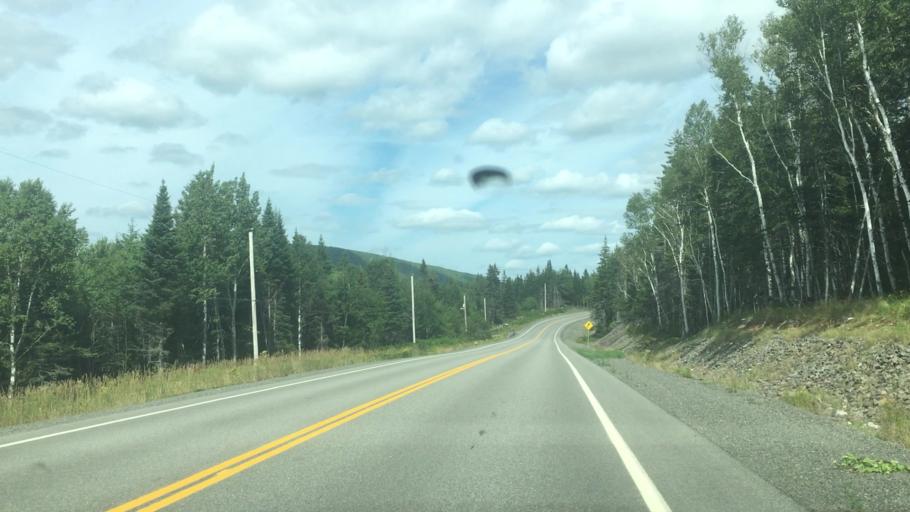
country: CA
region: Nova Scotia
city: Sydney Mines
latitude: 46.3241
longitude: -60.6066
